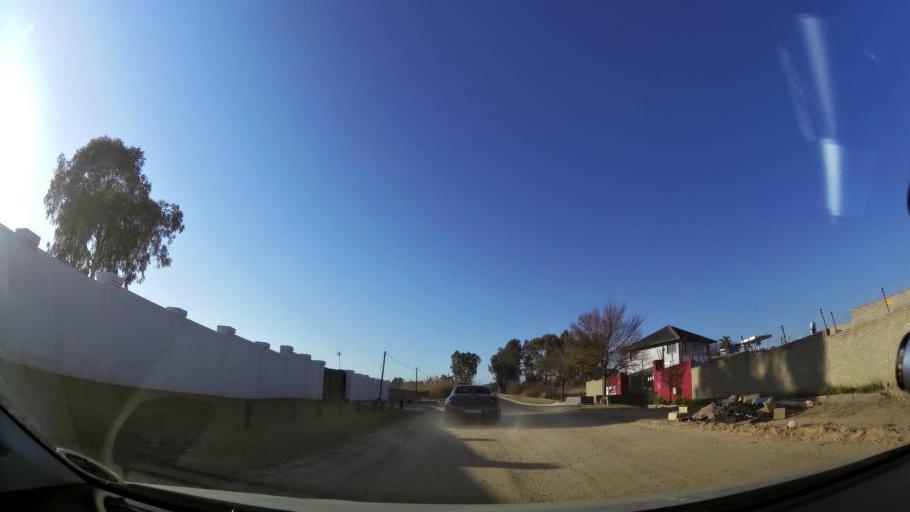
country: ZA
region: Gauteng
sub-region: City of Johannesburg Metropolitan Municipality
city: Midrand
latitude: -26.0297
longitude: 28.1365
